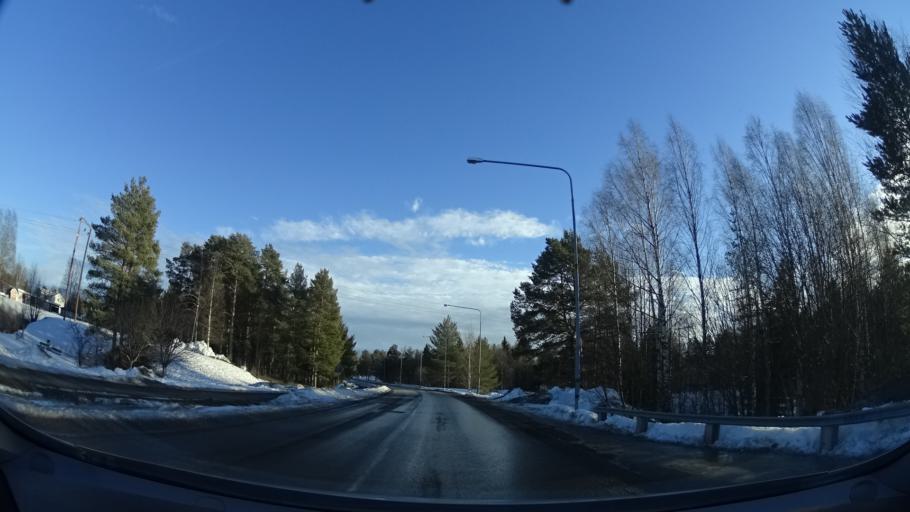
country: SE
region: Vaesterbotten
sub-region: Skelleftea Kommun
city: Byske
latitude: 64.9513
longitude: 21.2180
